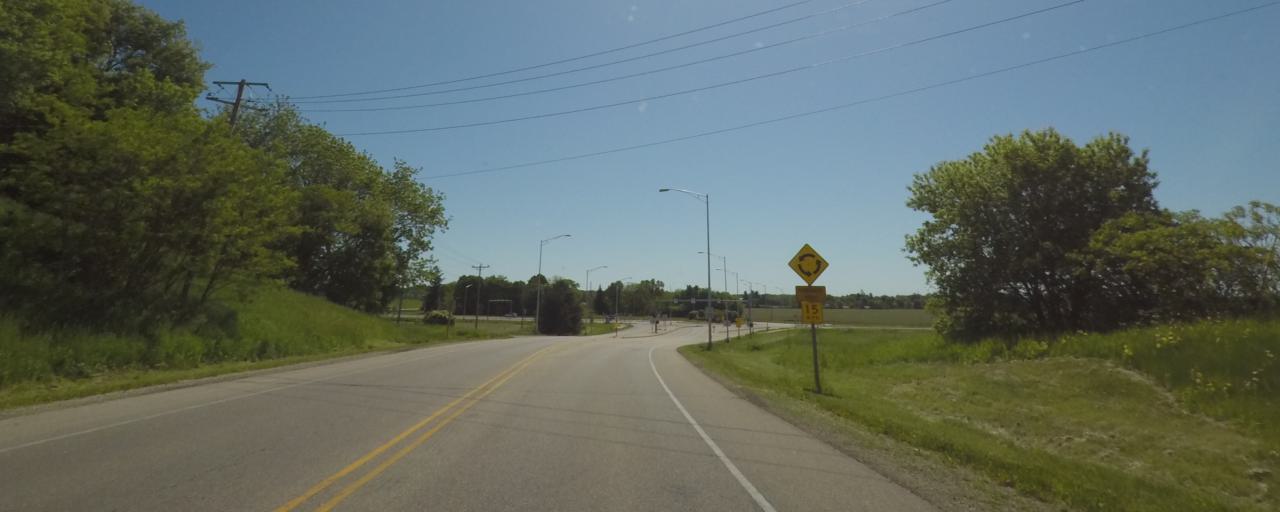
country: US
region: Wisconsin
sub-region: Dane County
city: Oregon
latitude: 42.9502
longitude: -89.3826
